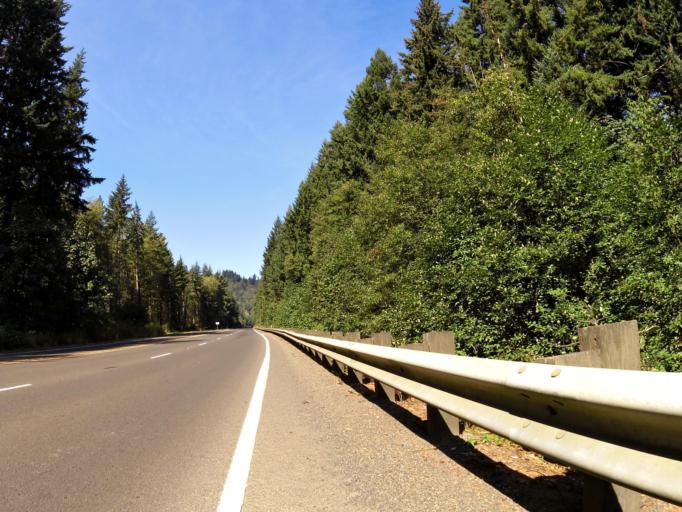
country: US
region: Washington
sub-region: Wahkiakum County
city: Cathlamet
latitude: 46.1538
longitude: -123.4156
